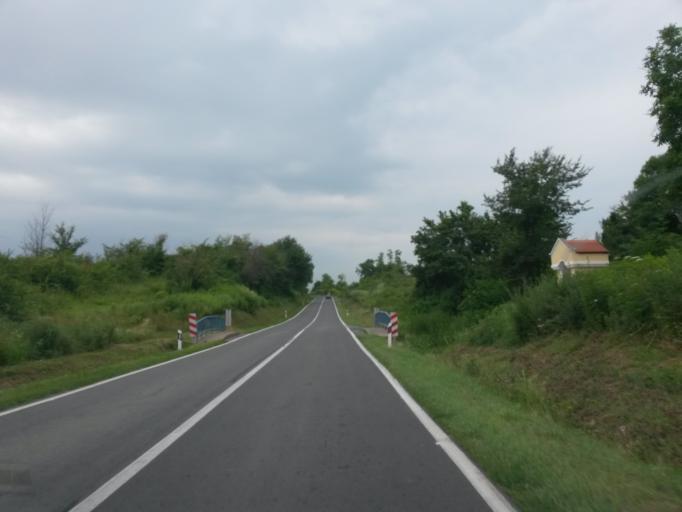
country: HR
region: Vukovarsko-Srijemska
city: Bapska
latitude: 45.2350
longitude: 19.2570
